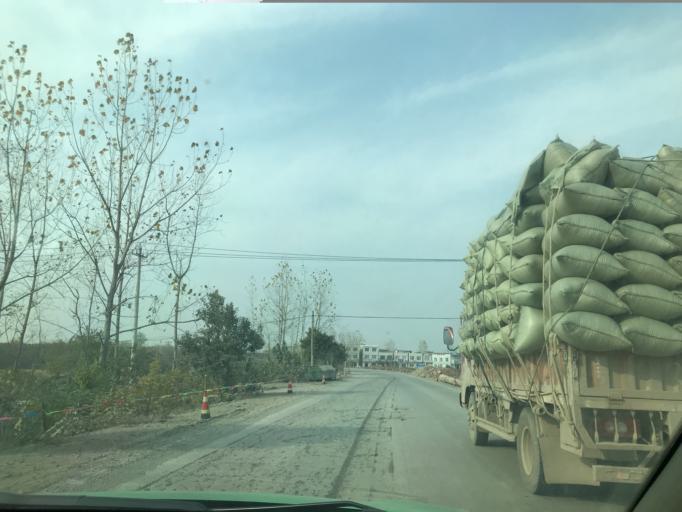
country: CN
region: Hubei
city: Tianmen
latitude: 30.7095
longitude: 113.1225
